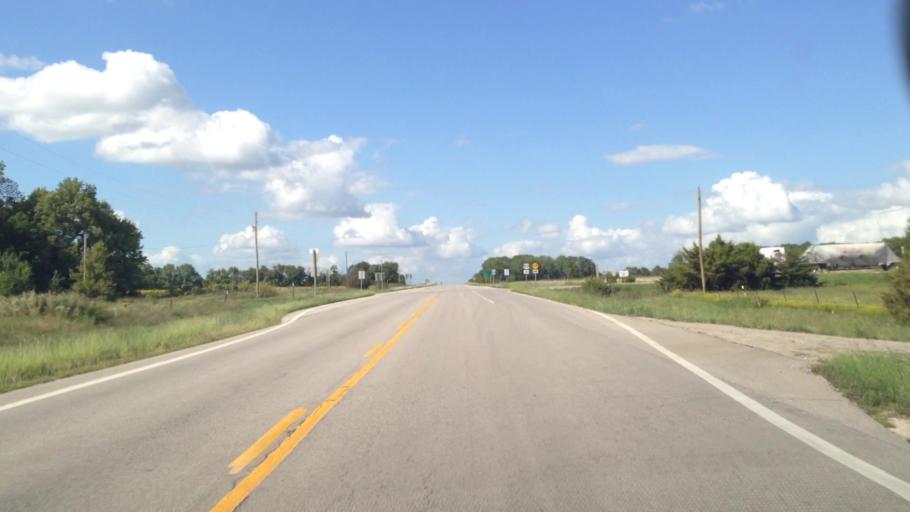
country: US
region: Kansas
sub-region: Neosho County
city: Erie
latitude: 37.7186
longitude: -95.1607
